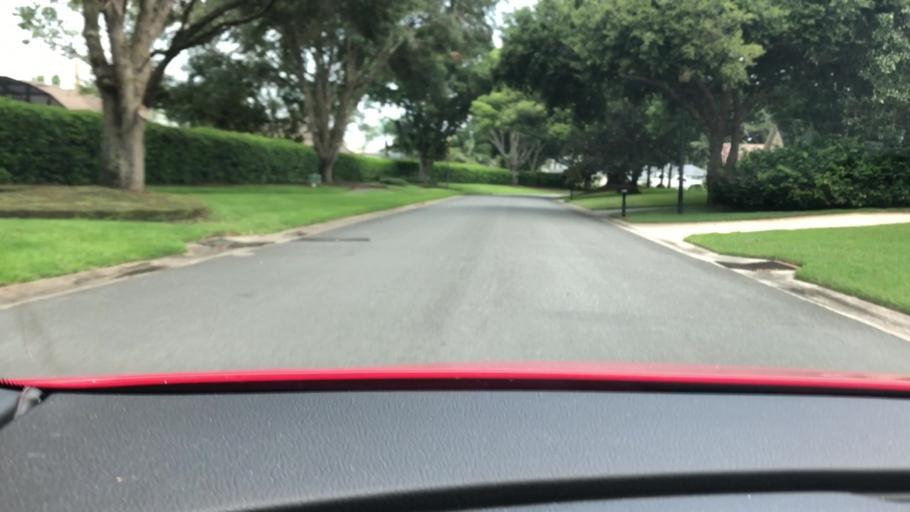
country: US
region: Florida
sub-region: Lake County
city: Mount Dora
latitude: 28.8462
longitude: -81.6353
